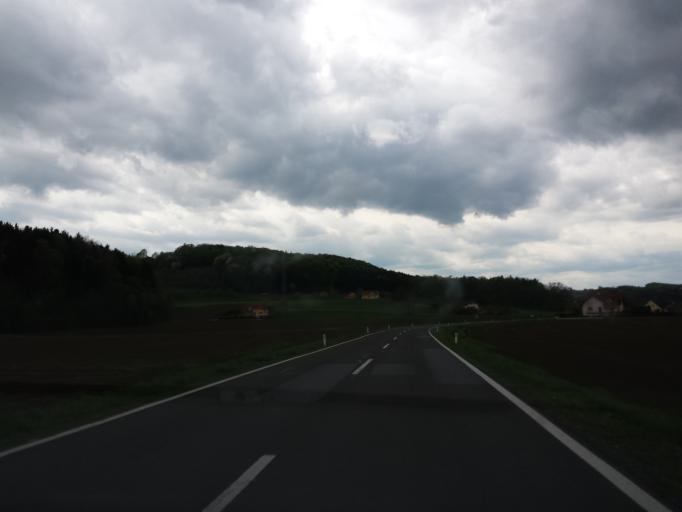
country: AT
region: Styria
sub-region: Politischer Bezirk Suedoststeiermark
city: Hatzendorf
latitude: 46.9875
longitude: 15.9821
